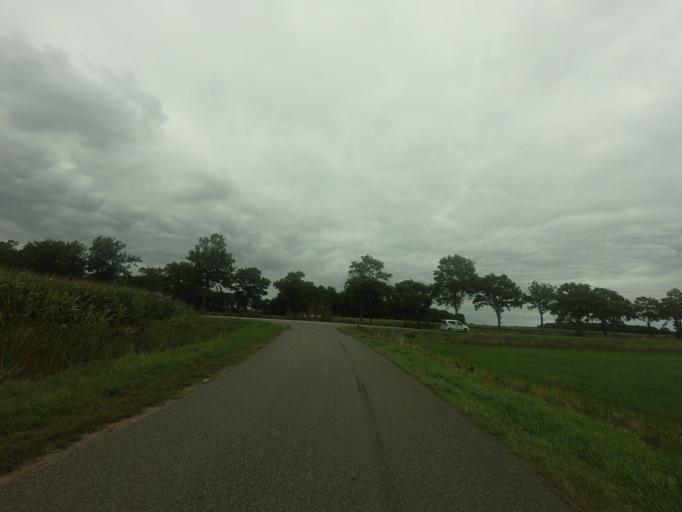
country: NL
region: Drenthe
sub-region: Gemeente Westerveld
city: Dwingeloo
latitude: 52.9693
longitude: 6.3294
